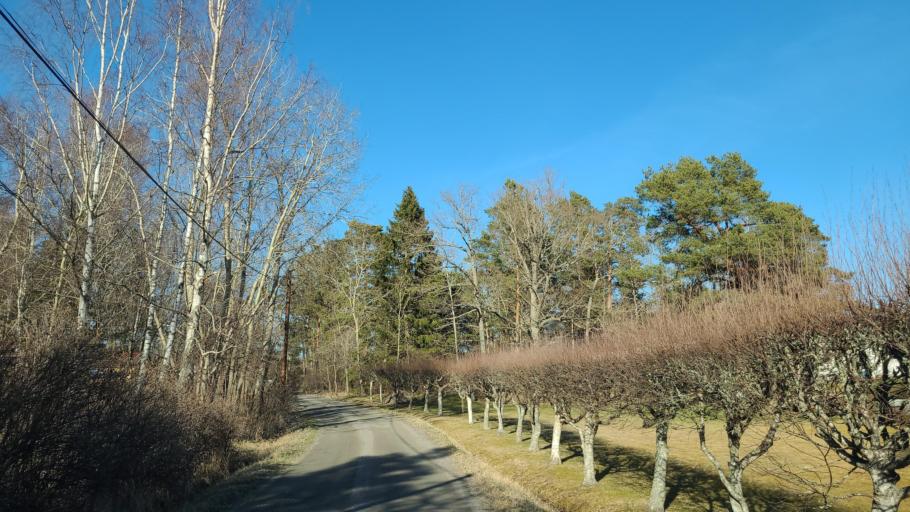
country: SE
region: Stockholm
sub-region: Varmdo Kommun
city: Holo
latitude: 59.3560
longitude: 18.6642
